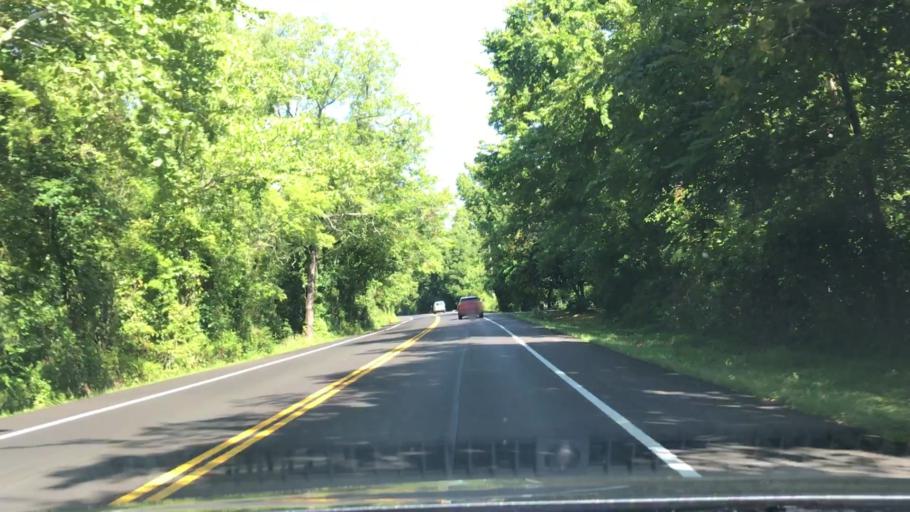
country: US
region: Tennessee
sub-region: Williamson County
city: Franklin
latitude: 35.9732
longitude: -86.8681
